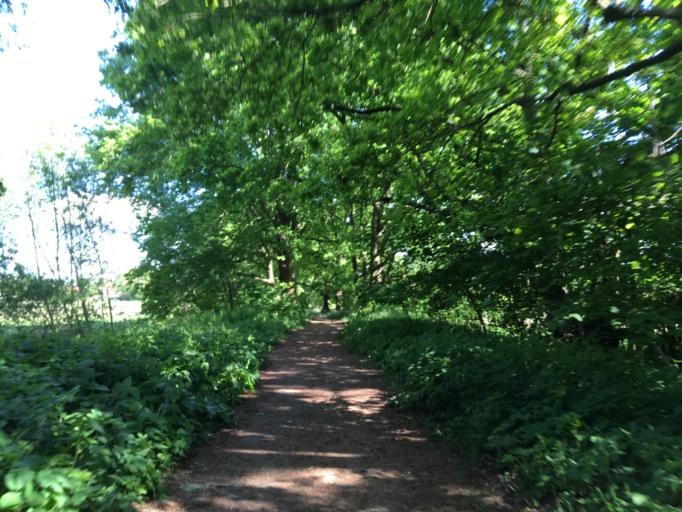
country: DE
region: Berlin
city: Buch
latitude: 52.6449
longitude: 13.5090
